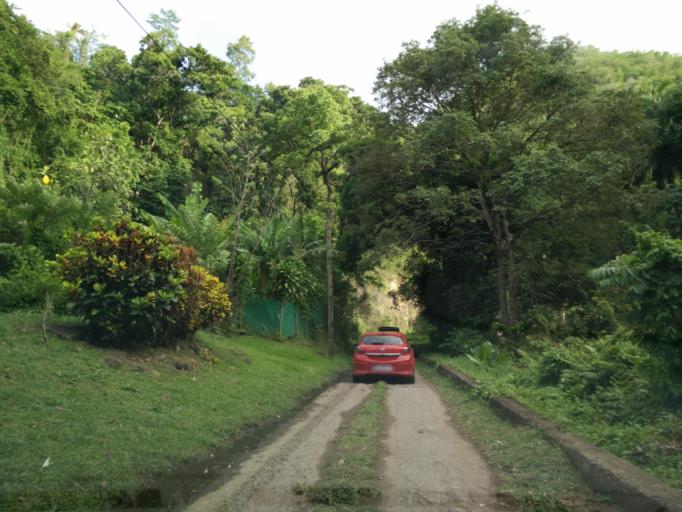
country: MQ
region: Martinique
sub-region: Martinique
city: Saint-Pierre
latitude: 14.7173
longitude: -61.1611
